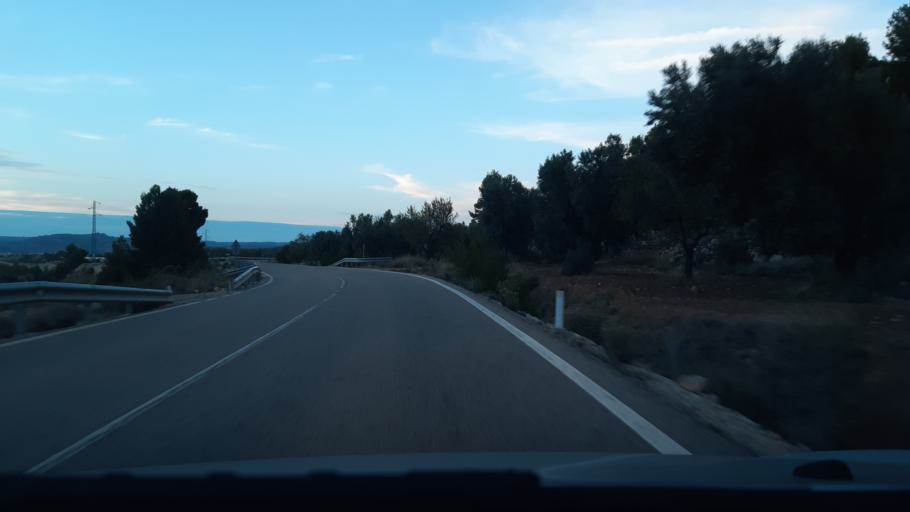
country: ES
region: Aragon
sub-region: Provincia de Teruel
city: Valderrobres
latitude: 40.8463
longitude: 0.1740
